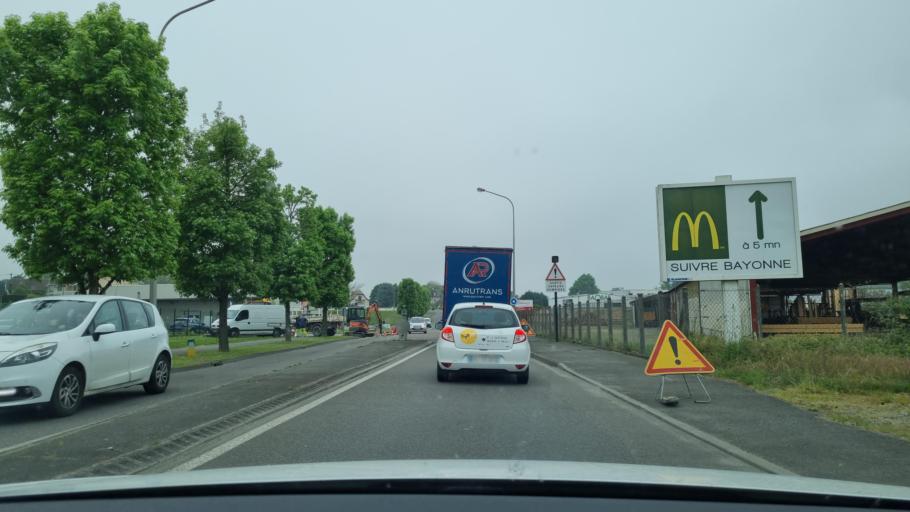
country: FR
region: Aquitaine
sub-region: Departement des Pyrenees-Atlantiques
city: Orthez
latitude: 43.4780
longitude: -0.7626
